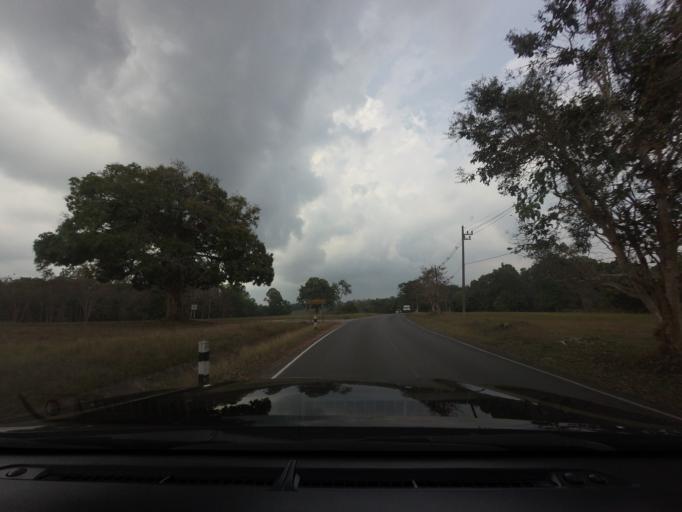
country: TH
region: Nakhon Nayok
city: Nakhon Nayok
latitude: 14.4119
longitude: 101.3713
